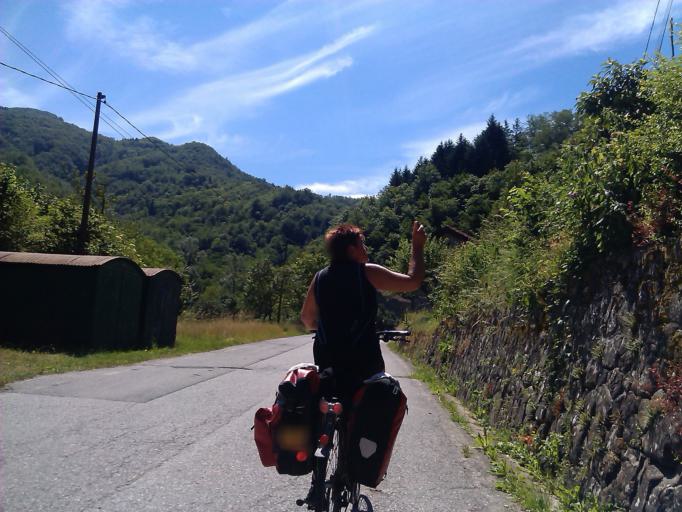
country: IT
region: Tuscany
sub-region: Provincia di Pistoia
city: Sambuca Pistoiese
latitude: 44.0778
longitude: 11.0505
